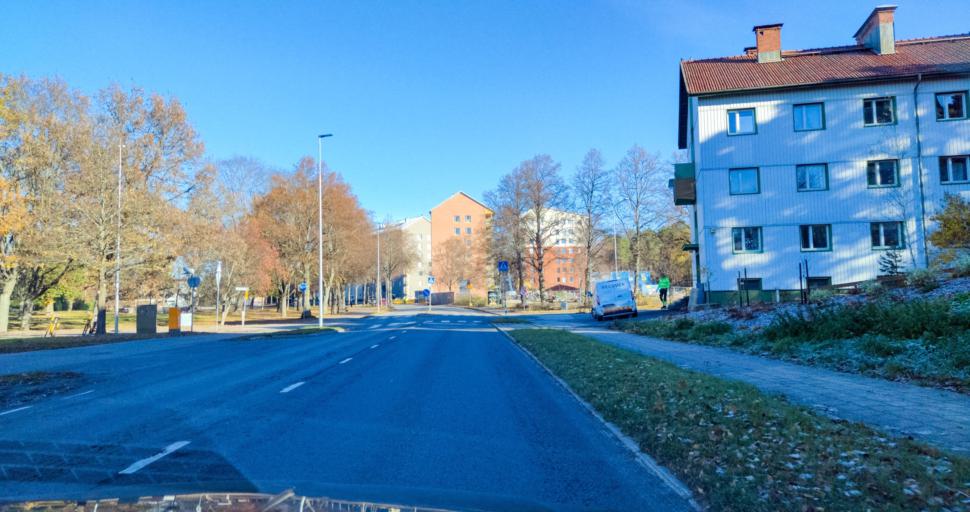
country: FI
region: Varsinais-Suomi
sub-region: Turku
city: Turku
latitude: 60.4374
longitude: 22.2672
